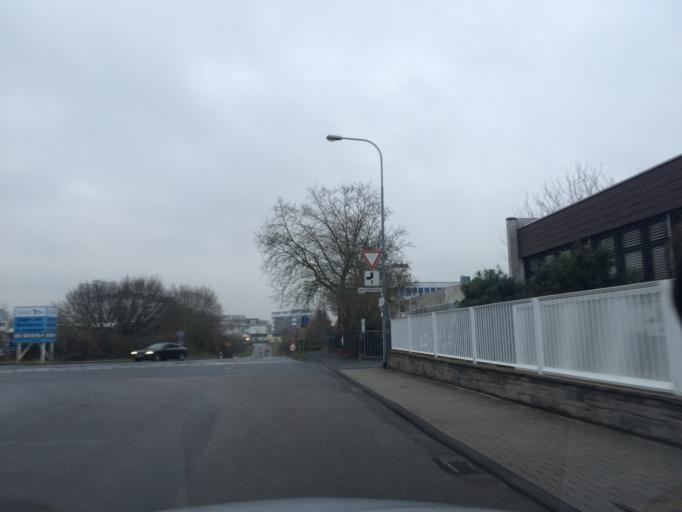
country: DE
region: Hesse
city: Langen
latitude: 49.9996
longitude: 8.6486
